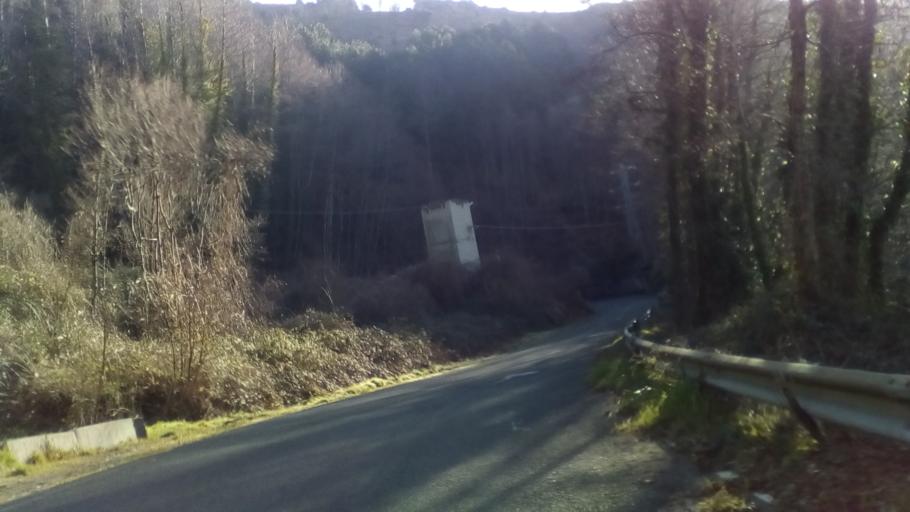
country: IT
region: Tuscany
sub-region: Provincia di Massa-Carrara
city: Montignoso
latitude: 44.0564
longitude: 10.2035
